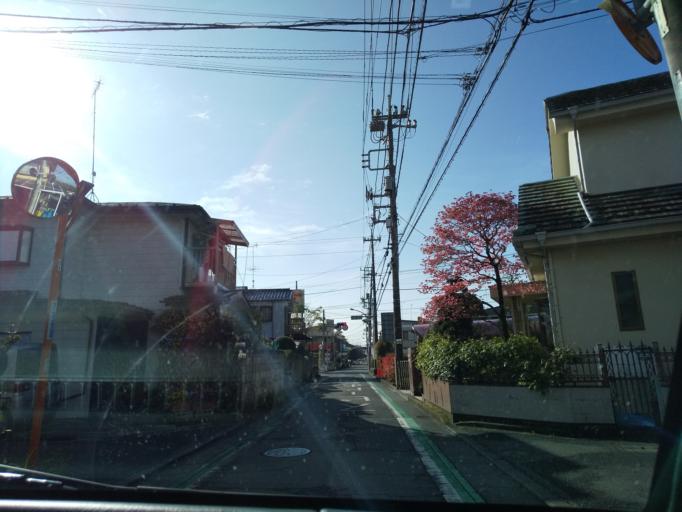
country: JP
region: Tokyo
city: Hachioji
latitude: 35.6739
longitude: 139.2872
